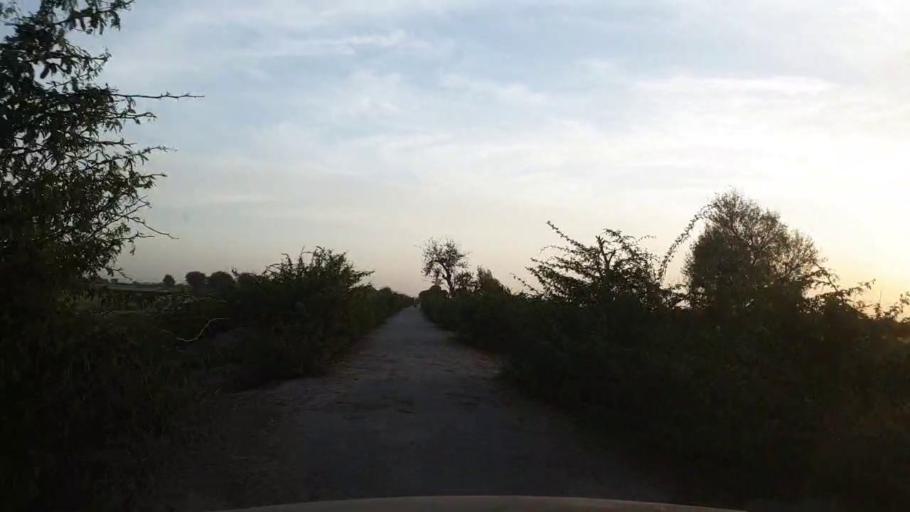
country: PK
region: Sindh
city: Kunri
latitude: 25.1107
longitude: 69.5620
